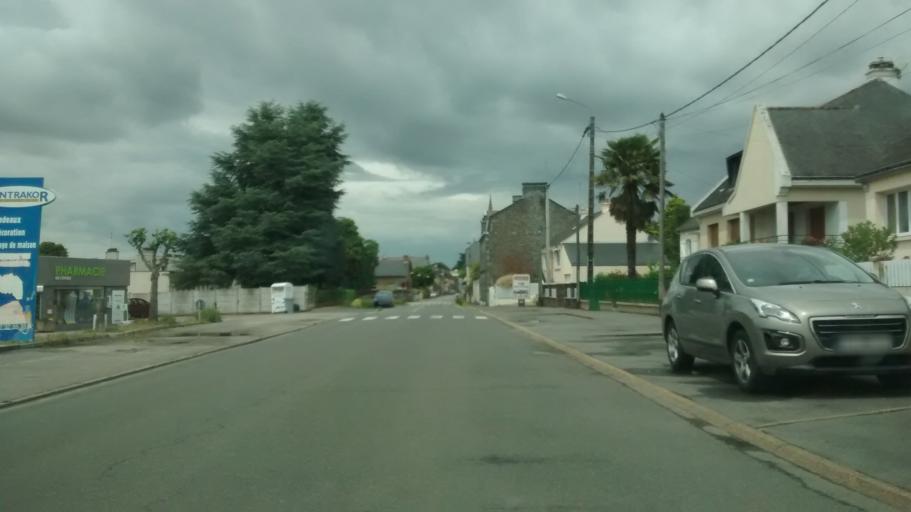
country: FR
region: Brittany
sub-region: Departement du Morbihan
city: Carentoir
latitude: 47.8133
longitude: -2.1307
